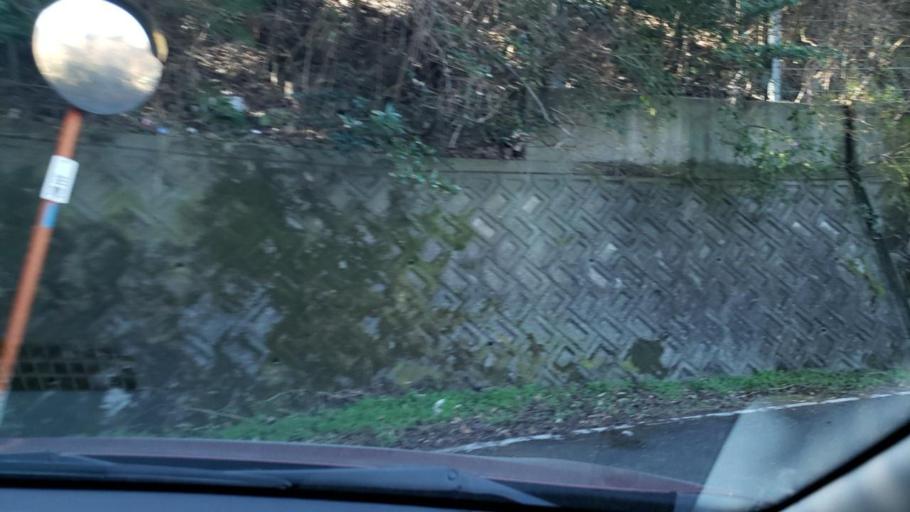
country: JP
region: Tokushima
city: Narutocho-mitsuishi
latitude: 34.1973
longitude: 134.5537
